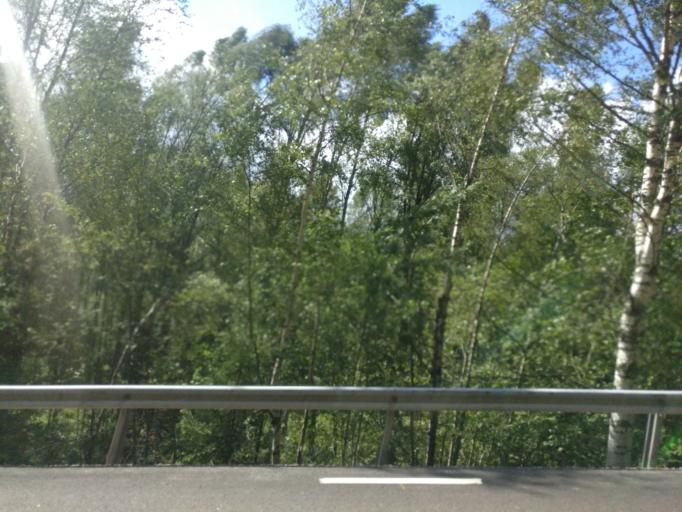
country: SE
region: Vaermland
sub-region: Hagfors Kommun
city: Ekshaerad
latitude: 60.3410
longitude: 13.3522
